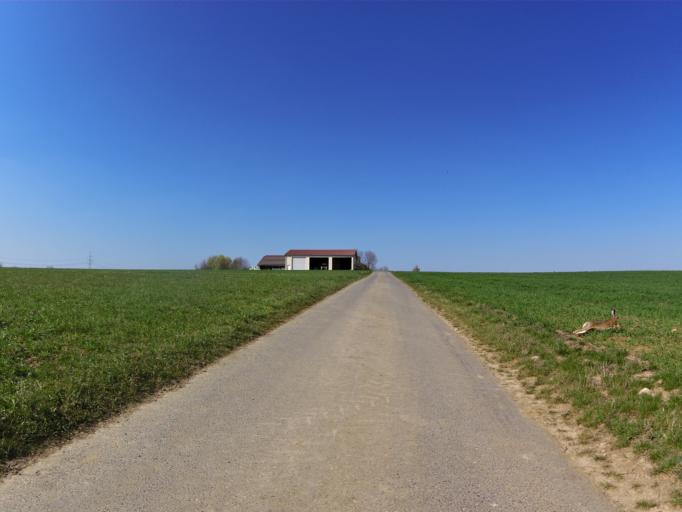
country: DE
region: Bavaria
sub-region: Regierungsbezirk Unterfranken
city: Biebelried
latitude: 49.8167
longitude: 10.0980
